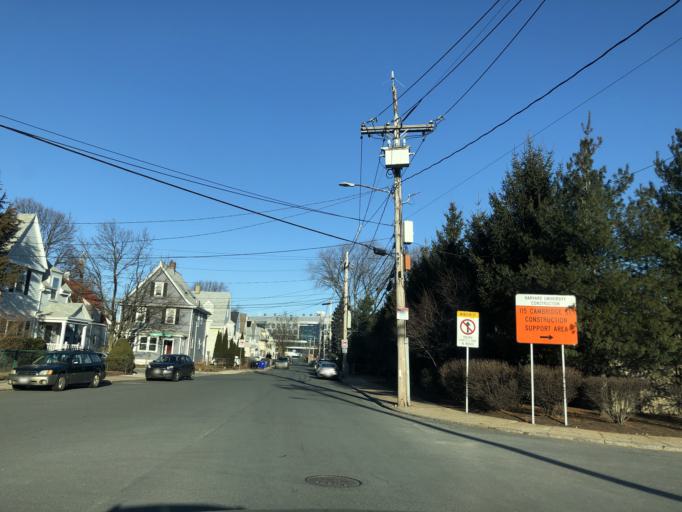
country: US
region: Massachusetts
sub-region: Middlesex County
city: Cambridge
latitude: 42.3594
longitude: -71.1233
